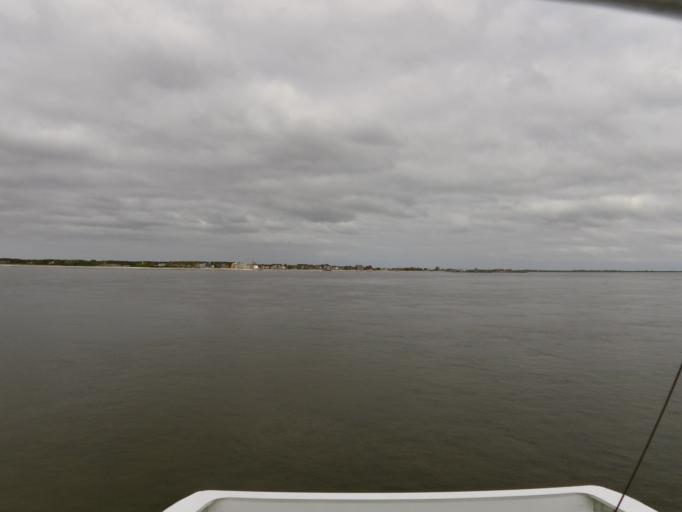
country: DE
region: Schleswig-Holstein
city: Wyk auf Fohr
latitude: 54.6785
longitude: 8.5920
